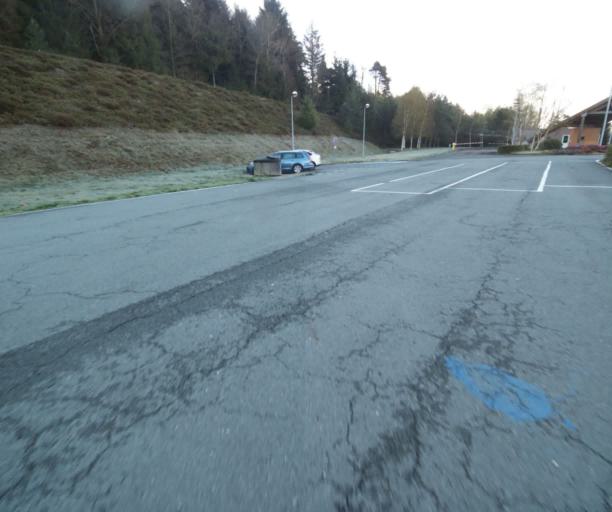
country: FR
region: Limousin
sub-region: Departement de la Correze
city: Correze
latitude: 45.3189
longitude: 1.8505
